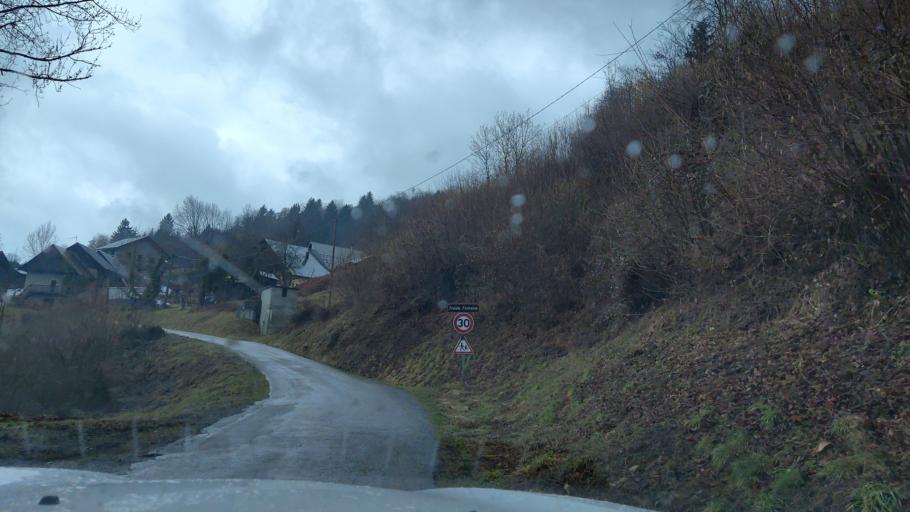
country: FR
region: Rhone-Alpes
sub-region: Departement de la Savoie
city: Aiton
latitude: 45.5054
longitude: 6.2850
